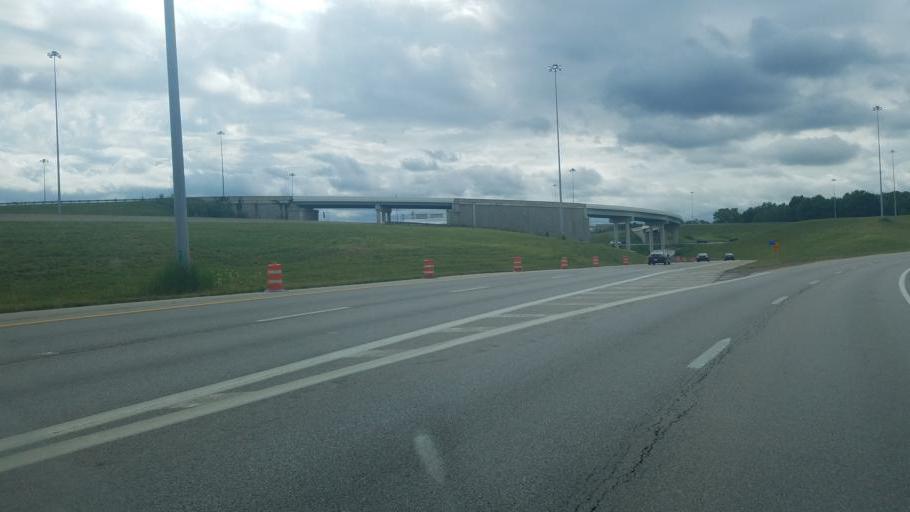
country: US
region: Ohio
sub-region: Franklin County
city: Huber Ridge
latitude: 40.0823
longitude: -82.9032
